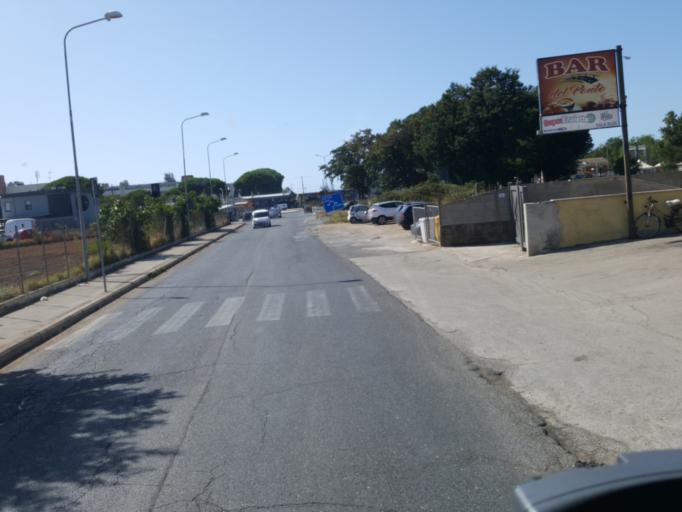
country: IT
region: Latium
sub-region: Citta metropolitana di Roma Capitale
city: Anzio
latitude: 41.5133
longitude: 12.6321
